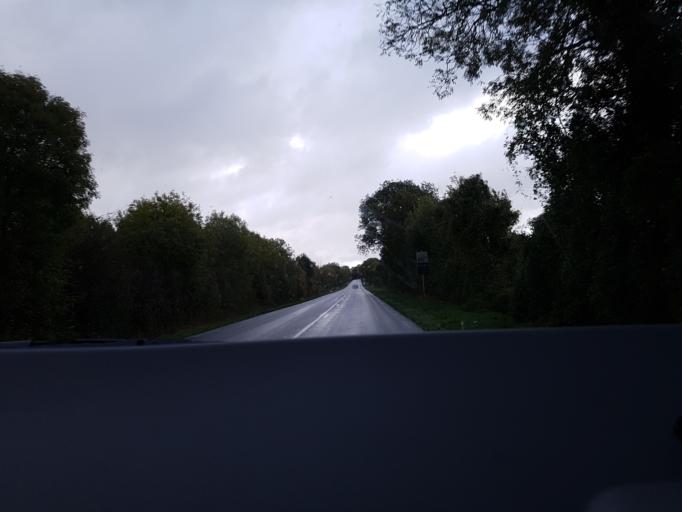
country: FR
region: Poitou-Charentes
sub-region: Departement des Deux-Sevres
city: Melle
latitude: 46.2038
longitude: -0.1569
